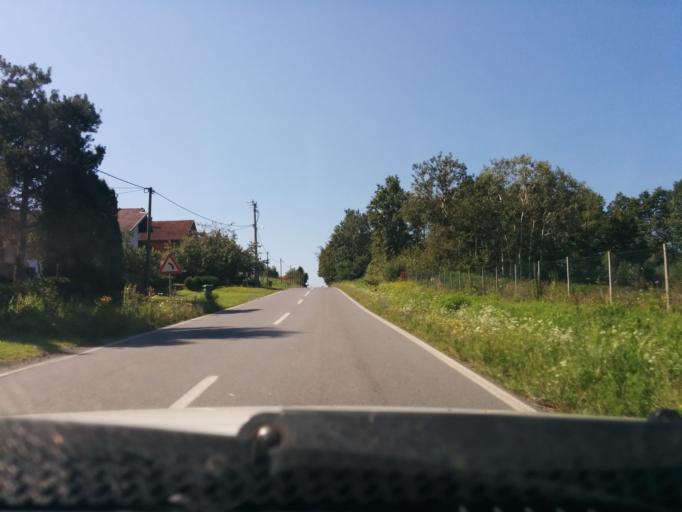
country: HR
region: Sisacko-Moslavacka
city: Lipovljani
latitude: 45.4014
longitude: 16.9045
